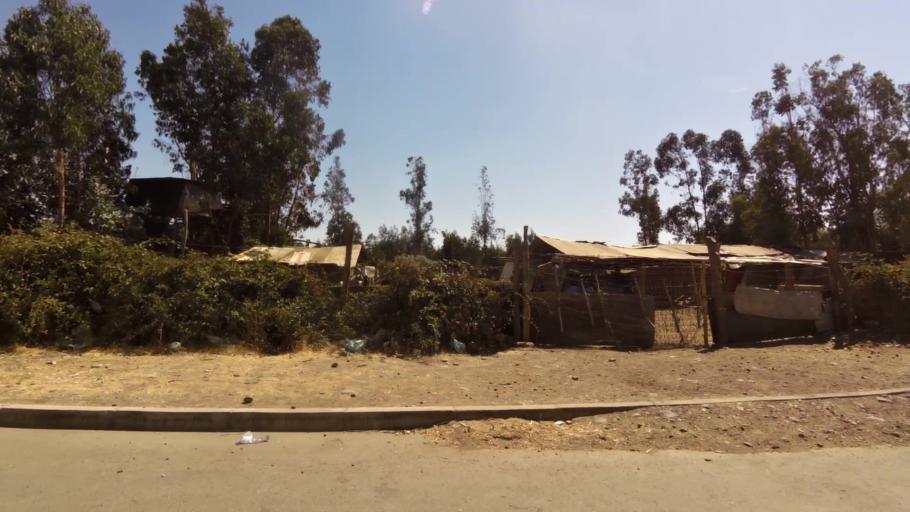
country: CL
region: Maule
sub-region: Provincia de Curico
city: Curico
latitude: -34.9598
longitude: -71.2345
